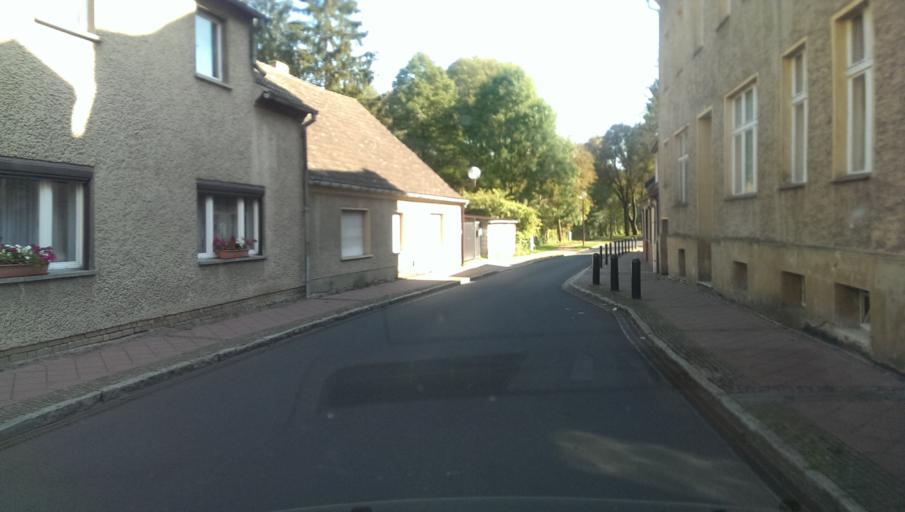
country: DE
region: Brandenburg
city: Teupitz
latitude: 52.1360
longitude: 13.6122
